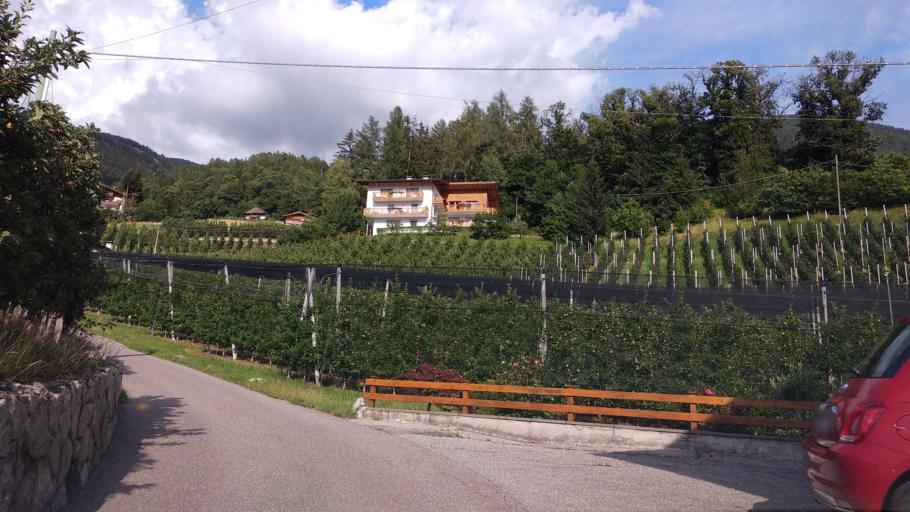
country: IT
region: Trentino-Alto Adige
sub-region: Bolzano
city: Scena
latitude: 46.6914
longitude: 11.1968
